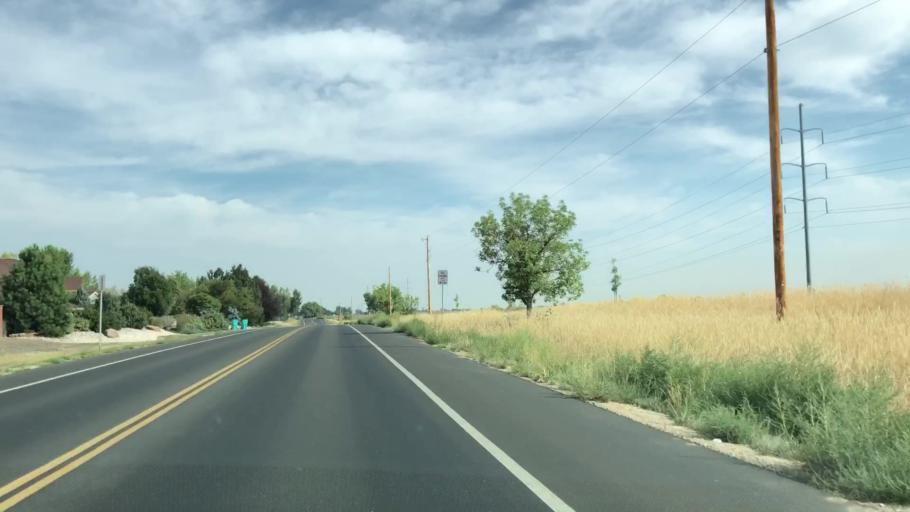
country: US
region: Colorado
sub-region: Larimer County
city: Loveland
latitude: 40.4346
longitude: -105.0454
